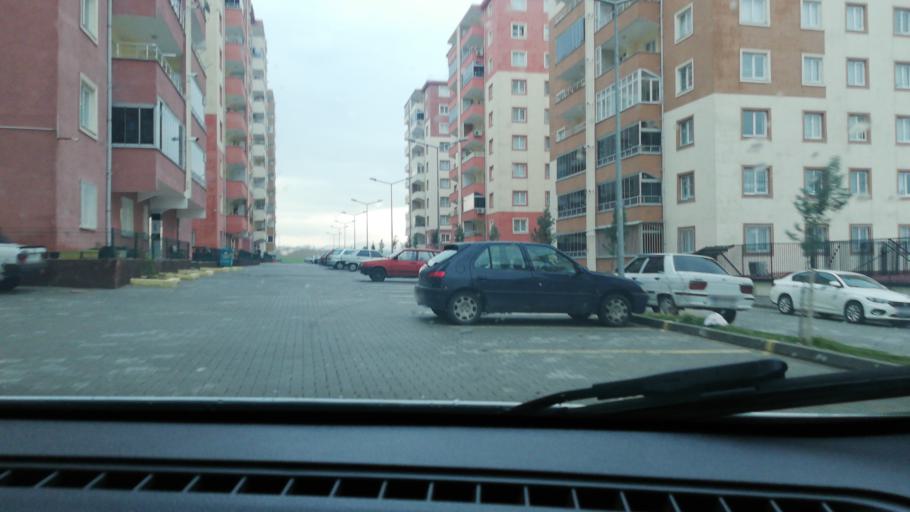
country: TR
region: Kahramanmaras
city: Kahramanmaras
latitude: 37.5802
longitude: 36.9986
